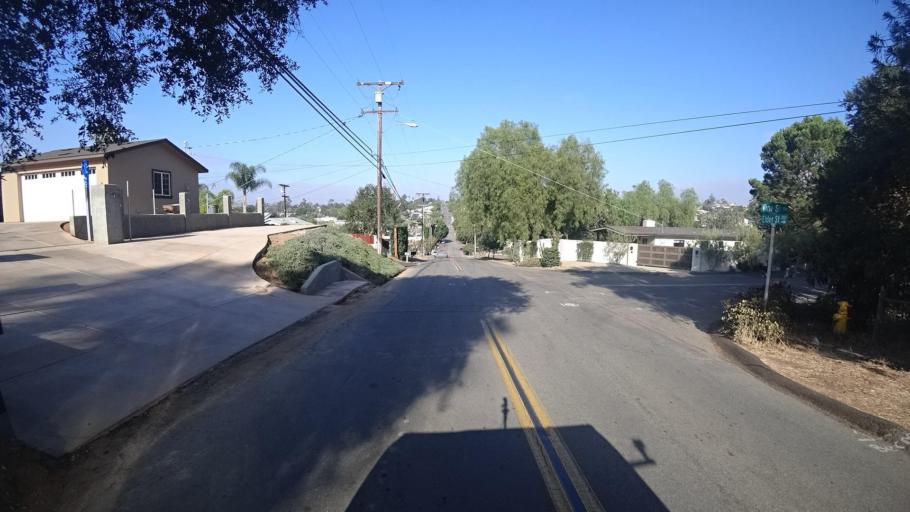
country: US
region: California
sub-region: San Diego County
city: Fallbrook
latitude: 33.3803
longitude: -117.2502
